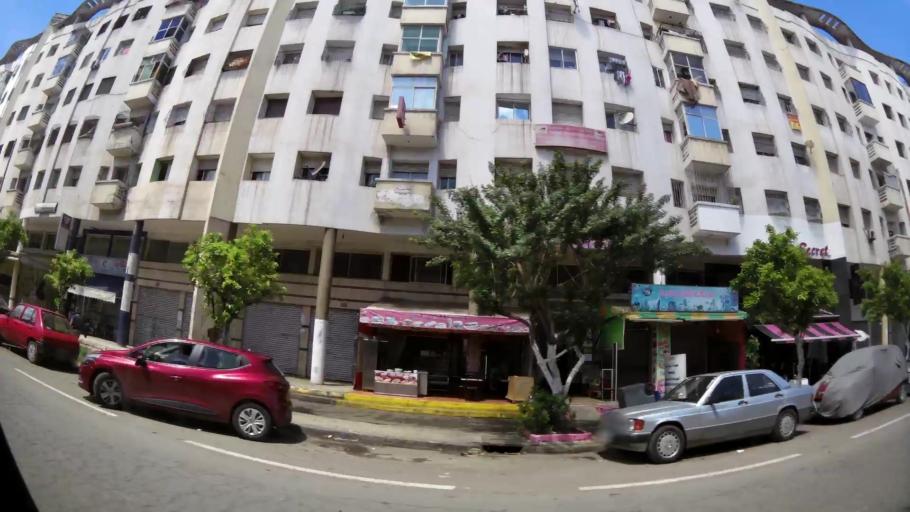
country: MA
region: Grand Casablanca
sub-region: Casablanca
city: Casablanca
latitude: 33.5628
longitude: -7.5588
